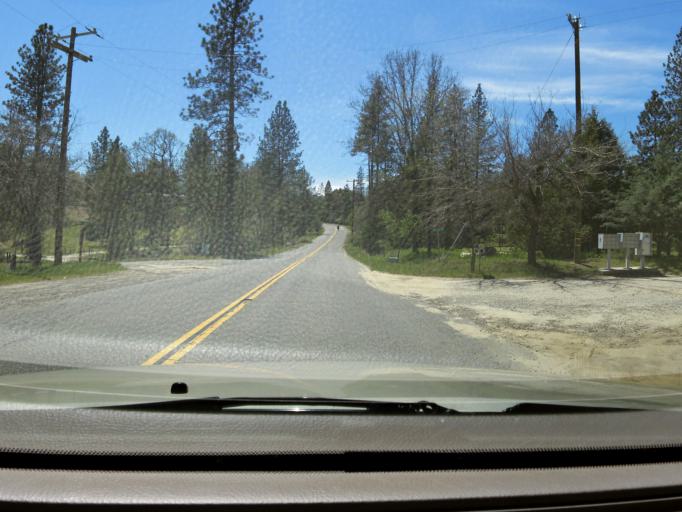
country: US
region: California
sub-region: Madera County
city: Oakhurst
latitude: 37.2370
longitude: -119.5489
